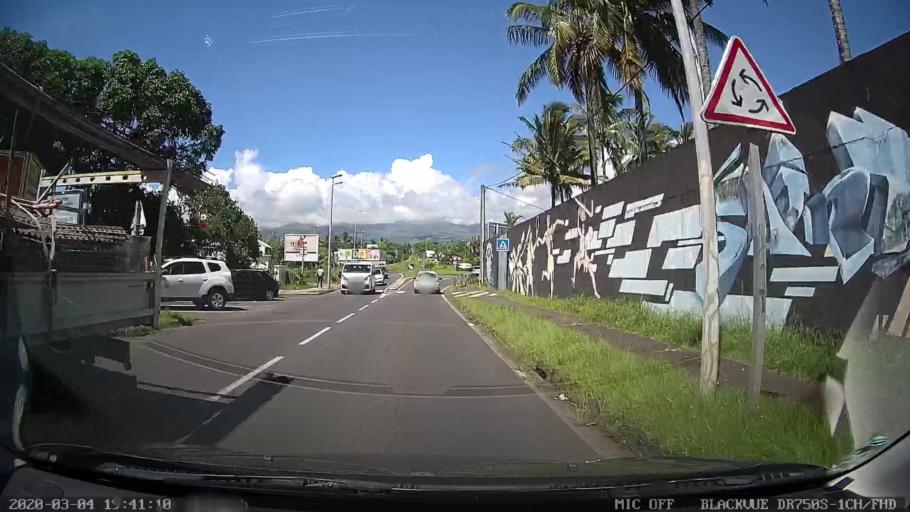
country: RE
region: Reunion
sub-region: Reunion
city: Saint-Benoit
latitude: -21.0467
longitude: 55.7180
